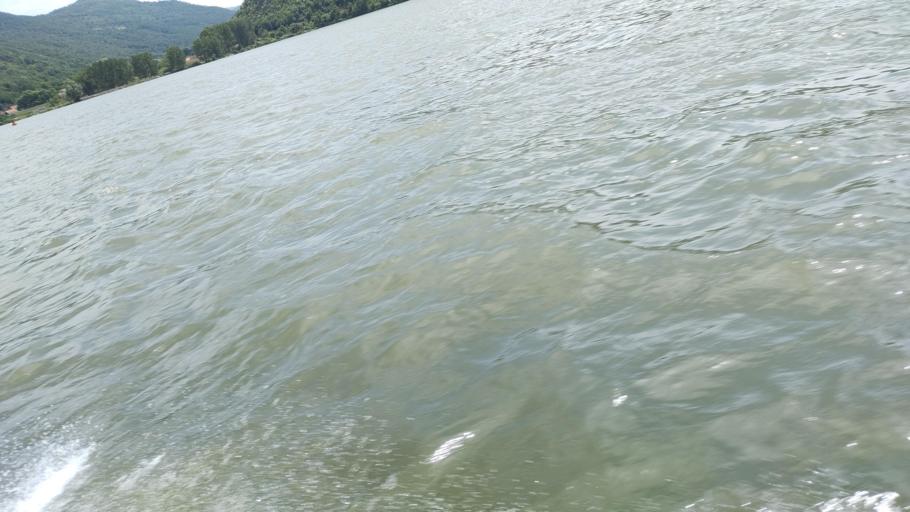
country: RO
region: Caras-Severin
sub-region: Comuna Berzasca
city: Liubcova
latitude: 44.6470
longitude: 21.9065
